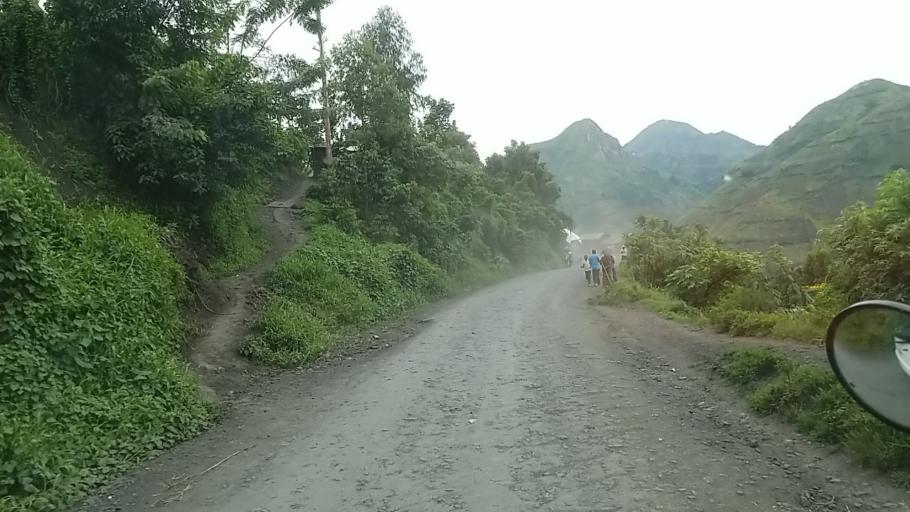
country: CD
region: Nord Kivu
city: Sake
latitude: -1.7587
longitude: 28.9868
